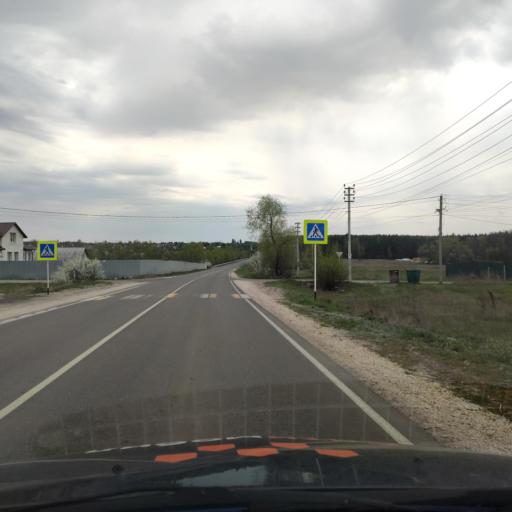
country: RU
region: Voronezj
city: Podgornoye
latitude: 51.8719
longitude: 39.1728
